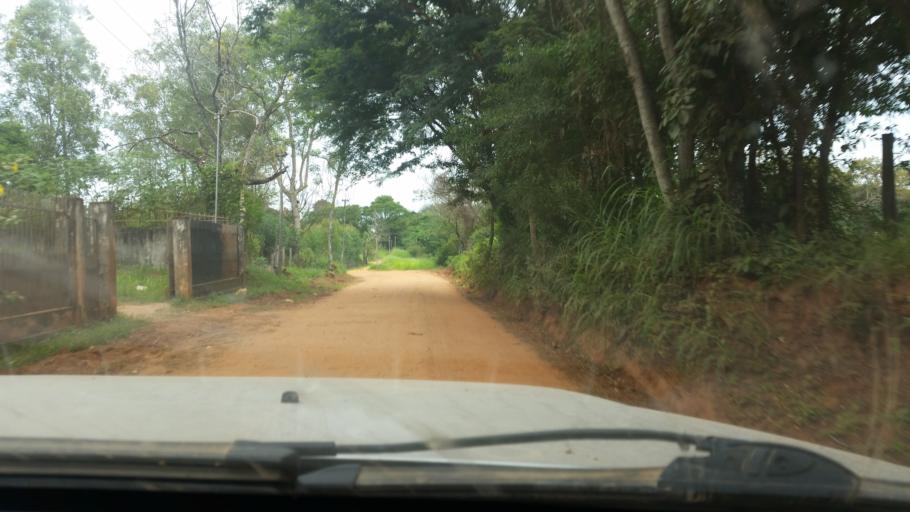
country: PY
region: Guaira
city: Independencia
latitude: -25.7043
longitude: -56.1920
